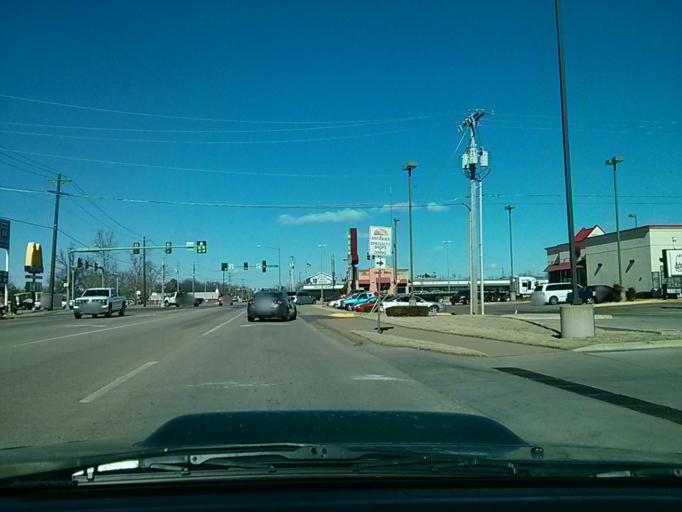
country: US
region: Oklahoma
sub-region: Tulsa County
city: Jenks
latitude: 36.0218
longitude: -95.9758
